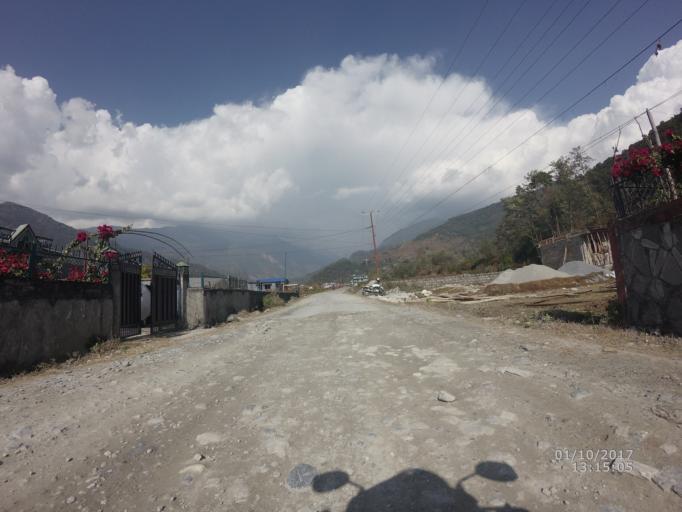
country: NP
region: Western Region
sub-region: Gandaki Zone
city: Pokhara
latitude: 28.3235
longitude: 83.9628
